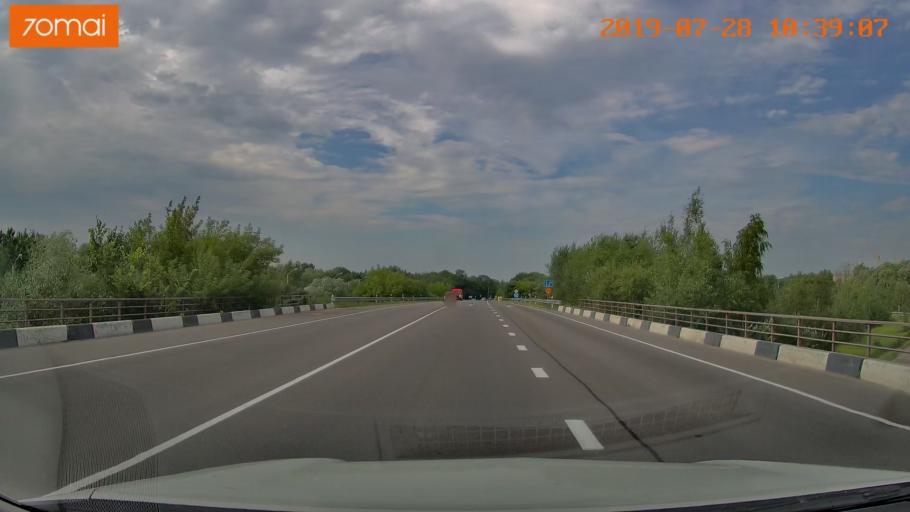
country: RU
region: Kaliningrad
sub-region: Gorod Kaliningrad
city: Kaliningrad
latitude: 54.7195
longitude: 20.3874
